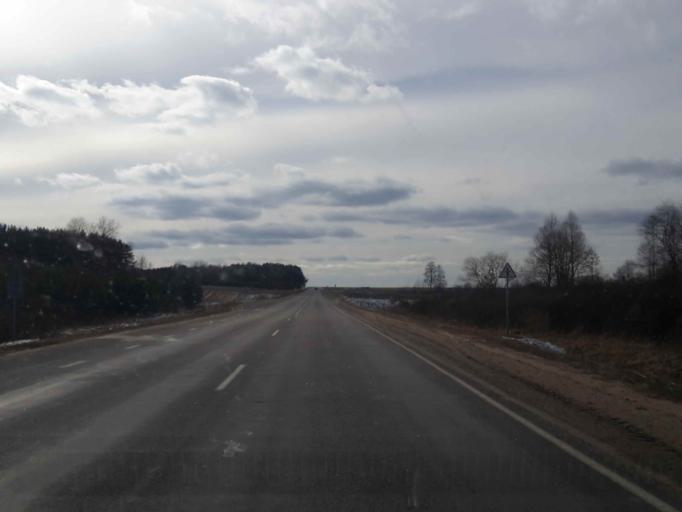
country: BY
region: Minsk
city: Myadzyel
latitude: 55.0332
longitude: 26.9757
